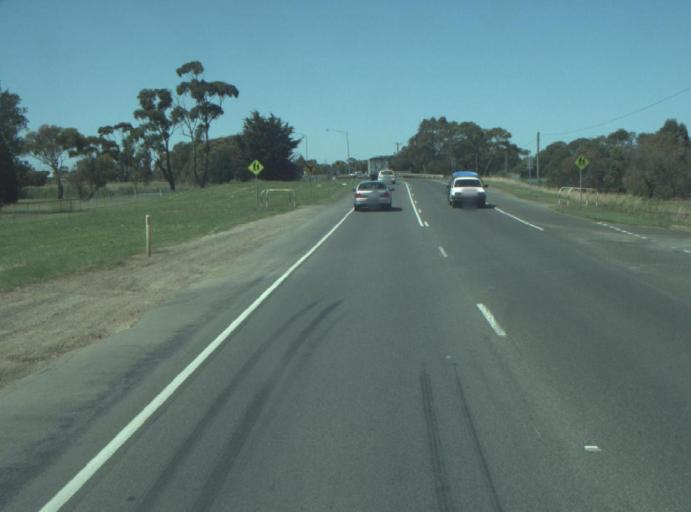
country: AU
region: Victoria
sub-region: Greater Geelong
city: Breakwater
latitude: -38.1844
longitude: 144.3544
